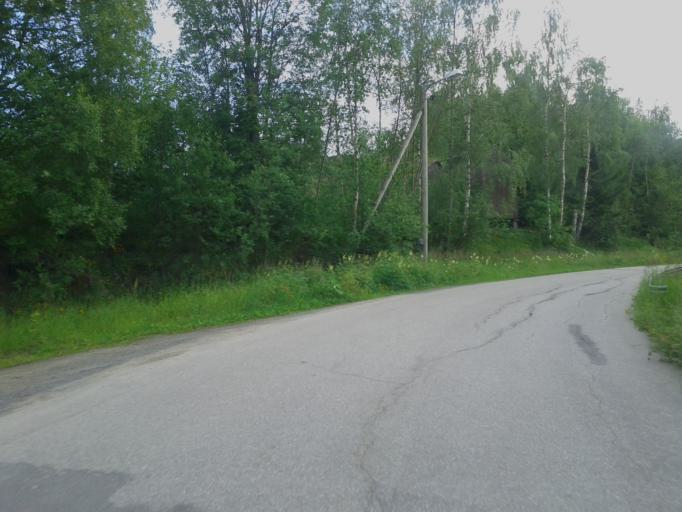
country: SE
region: Vaesternorrland
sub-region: OErnskoeldsviks Kommun
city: Ornskoldsvik
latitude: 63.2689
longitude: 18.8096
